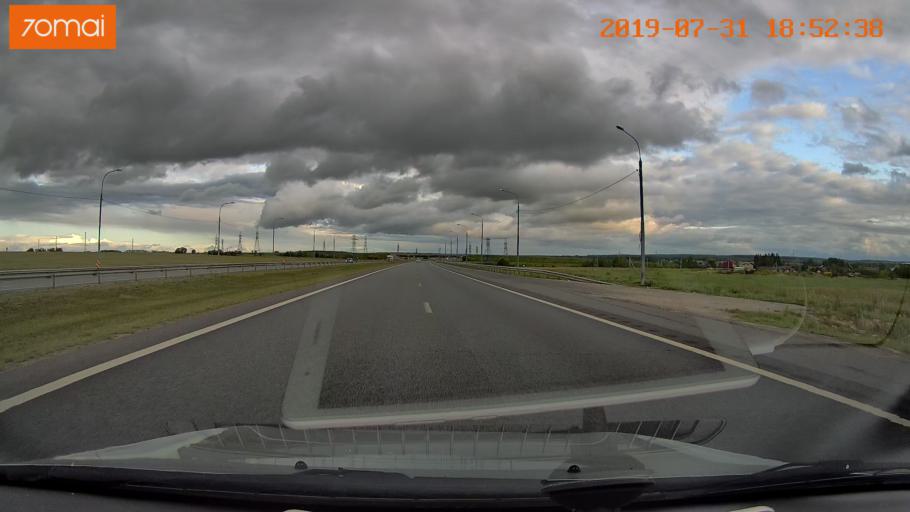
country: RU
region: Moskovskaya
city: Voskresensk
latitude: 55.2119
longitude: 38.6362
